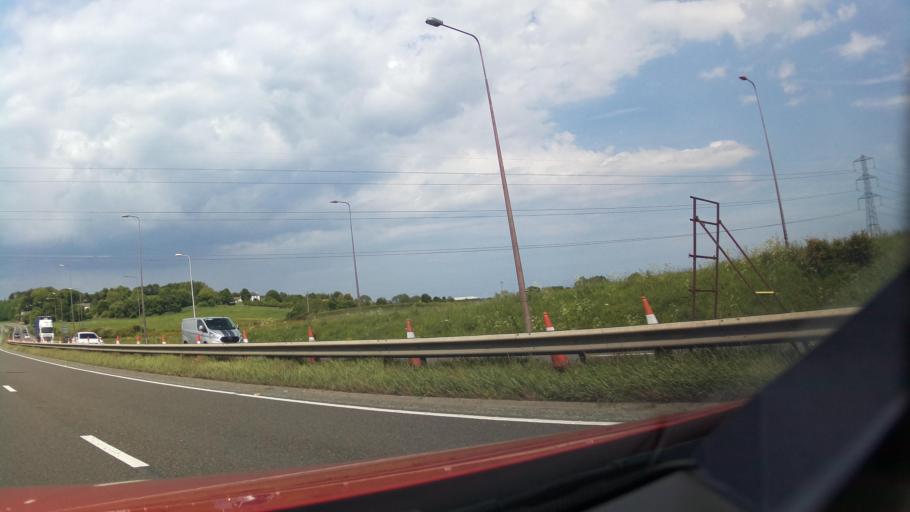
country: GB
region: England
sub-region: Hartlepool
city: Elwick
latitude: 54.7033
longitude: -1.3170
